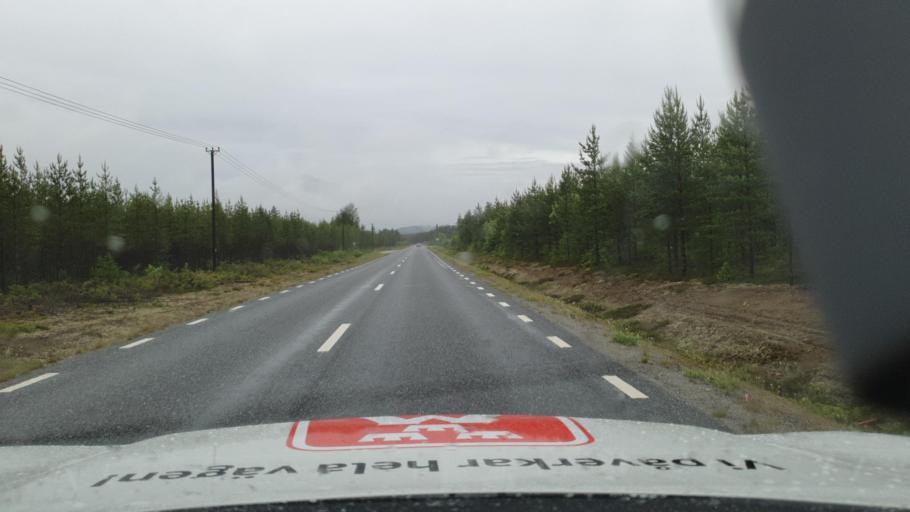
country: SE
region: Vaesterbotten
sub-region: Asele Kommun
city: Asele
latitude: 63.9587
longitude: 17.2698
